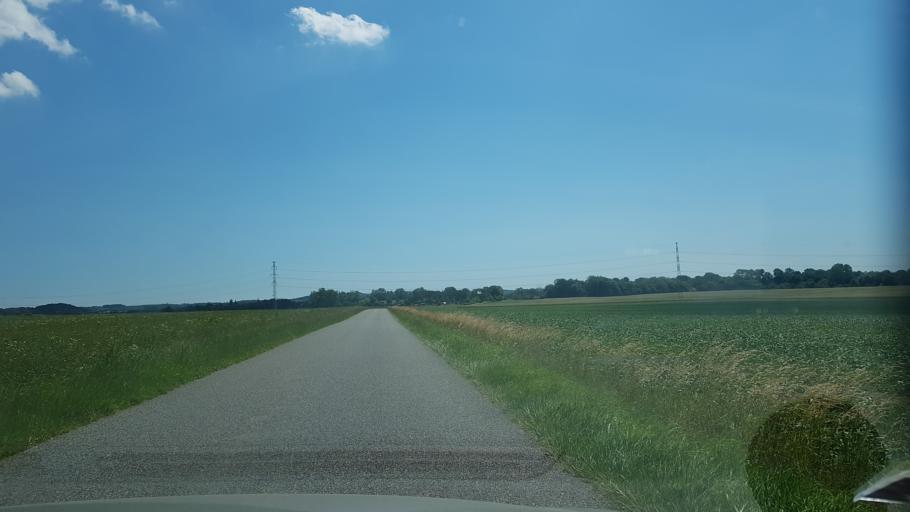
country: DK
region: Zealand
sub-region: Kalundborg Kommune
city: Svebolle
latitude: 55.6929
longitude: 11.3010
